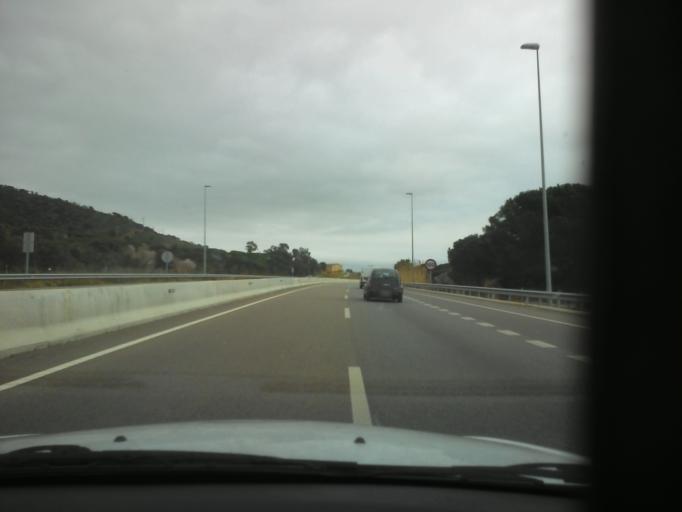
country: ES
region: Catalonia
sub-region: Provincia de Girona
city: Castell-Platja d'Aro
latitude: 41.8169
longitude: 3.0446
